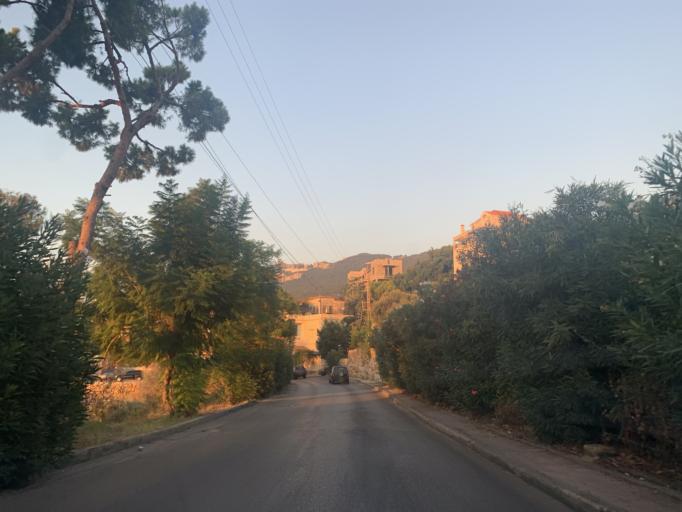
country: LB
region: Mont-Liban
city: Djounie
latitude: 33.9697
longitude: 35.6247
